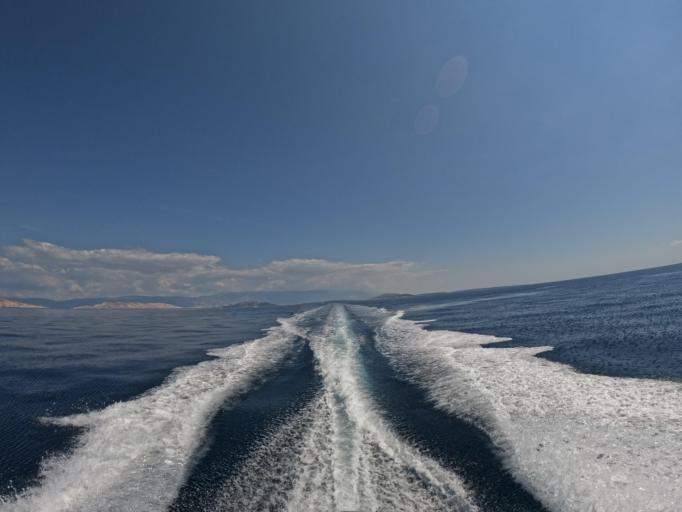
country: HR
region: Primorsko-Goranska
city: Punat
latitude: 44.9064
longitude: 14.6005
